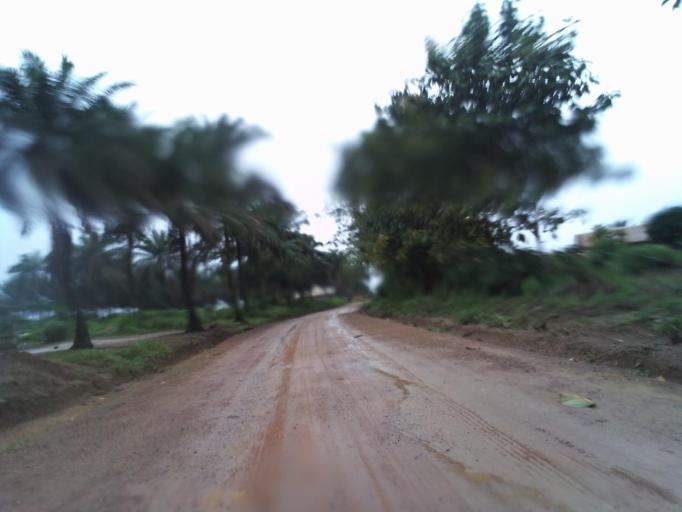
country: SL
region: Eastern Province
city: Kenema
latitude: 7.8765
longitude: -11.1552
